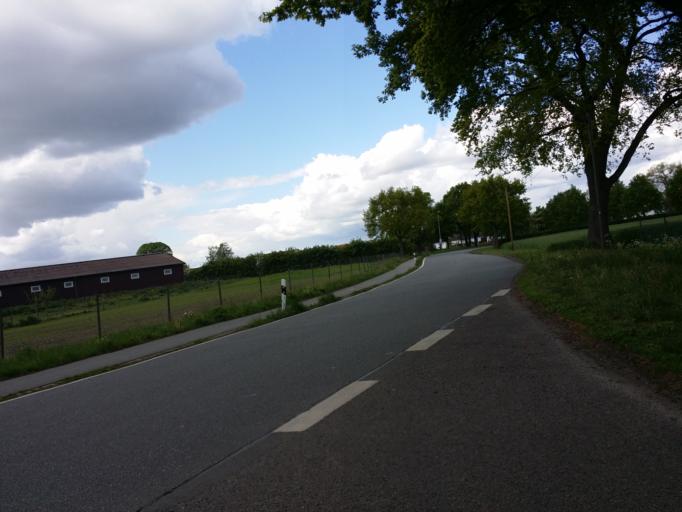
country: DE
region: Lower Saxony
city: Stuhr
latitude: 52.9921
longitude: 8.7545
